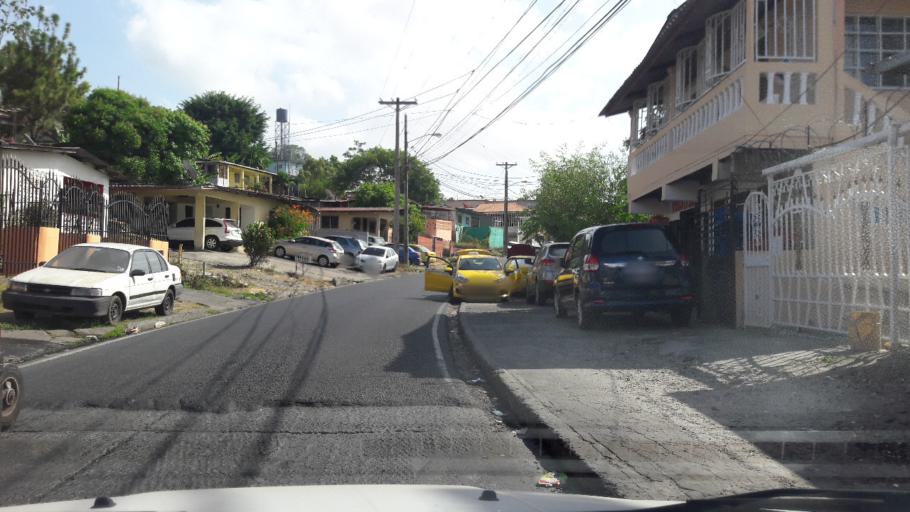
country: PA
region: Panama
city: San Miguelito
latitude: 9.0432
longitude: -79.4941
